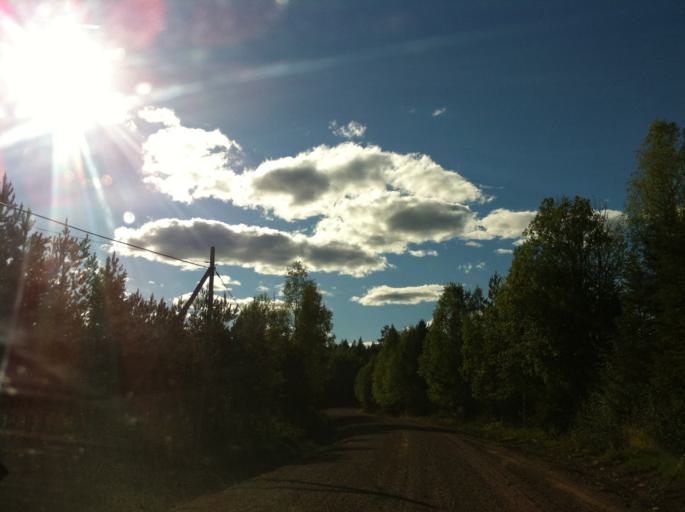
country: SE
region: Dalarna
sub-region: Leksand Municipality
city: Siljansnas
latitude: 60.7803
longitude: 14.8296
